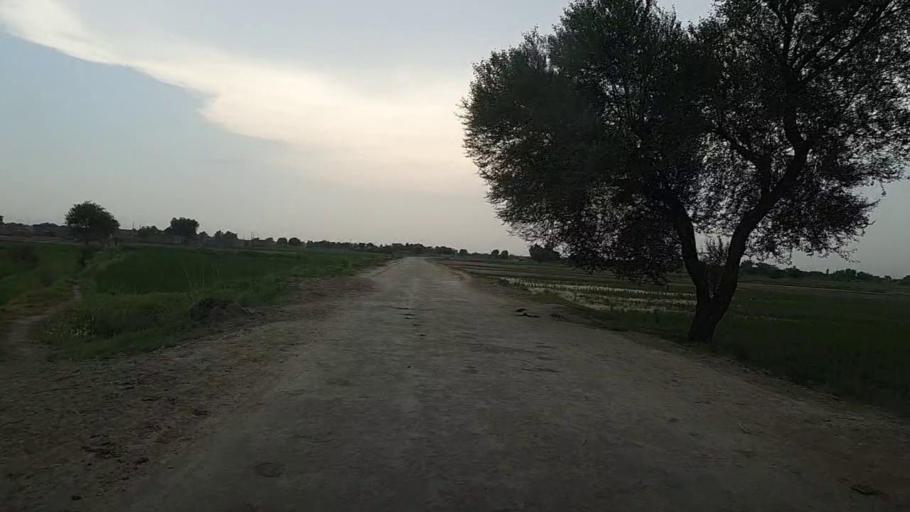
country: PK
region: Sindh
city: Khanpur
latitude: 27.8469
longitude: 69.4550
